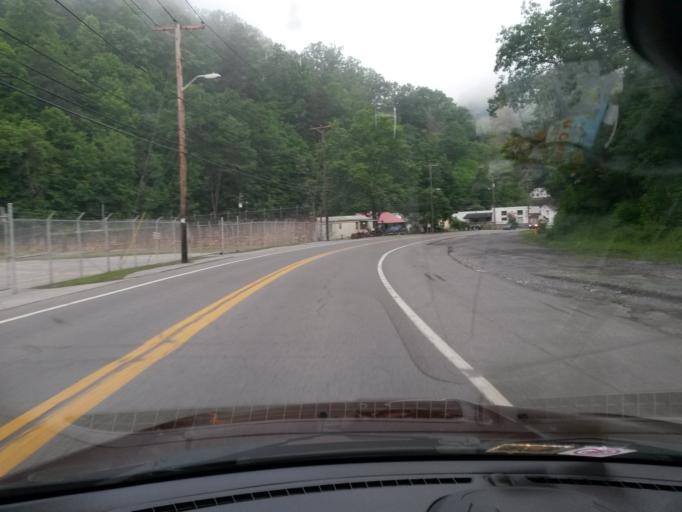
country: US
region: West Virginia
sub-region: McDowell County
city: Welch
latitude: 37.4398
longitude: -81.5764
